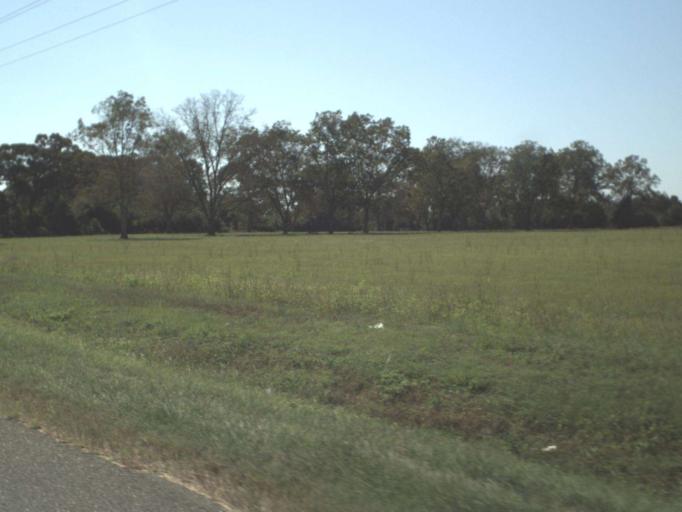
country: US
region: Florida
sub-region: Okaloosa County
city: Crestview
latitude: 30.8484
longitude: -86.5288
